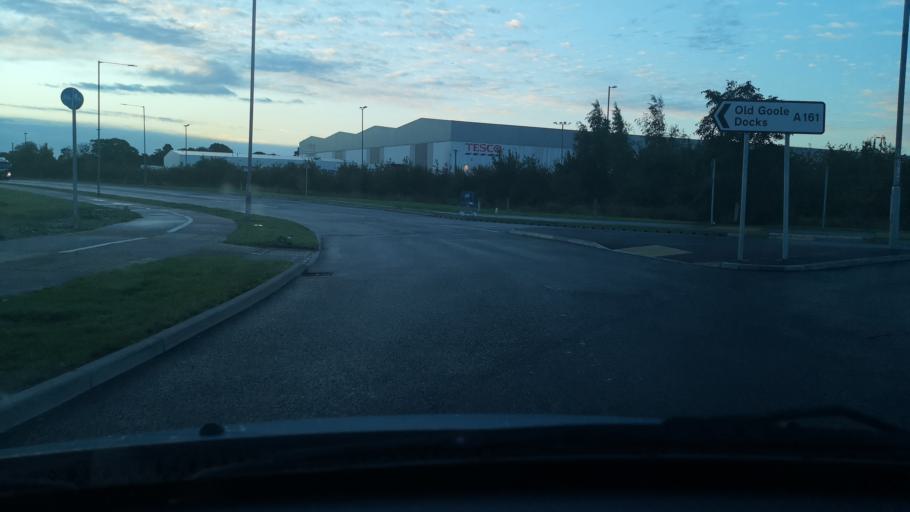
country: GB
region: England
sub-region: East Riding of Yorkshire
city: Airmyn
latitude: 53.7004
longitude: -0.9051
